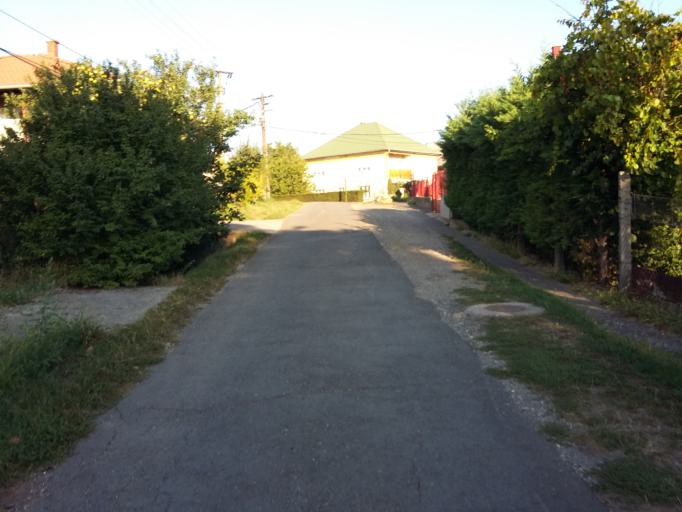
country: HU
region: Borsod-Abauj-Zemplen
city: Bekecs
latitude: 48.1592
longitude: 21.1800
